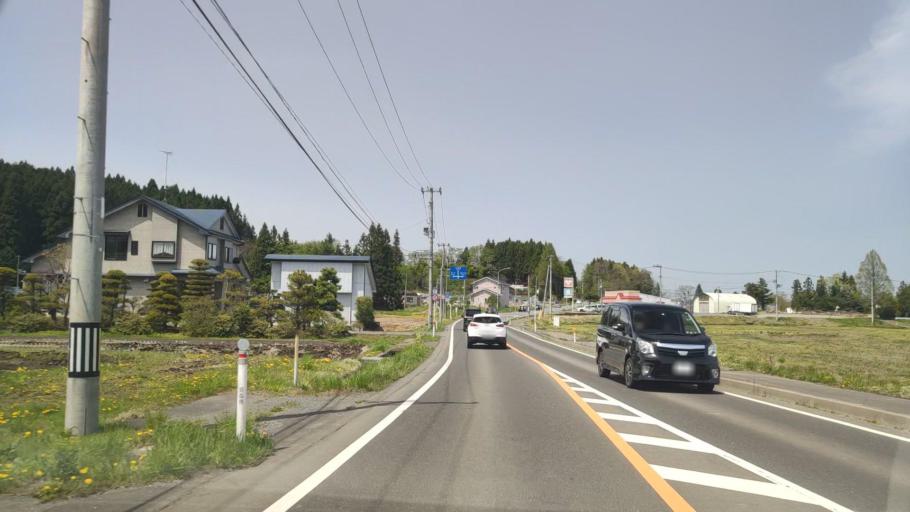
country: JP
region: Aomori
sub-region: Misawa Shi
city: Inuotose
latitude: 40.5869
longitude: 141.3539
